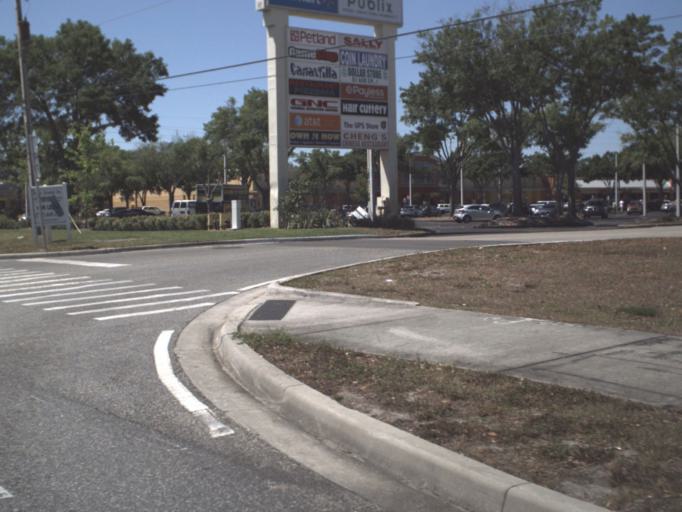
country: US
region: Florida
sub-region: Orange County
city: Conway
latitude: 28.5047
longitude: -81.3104
